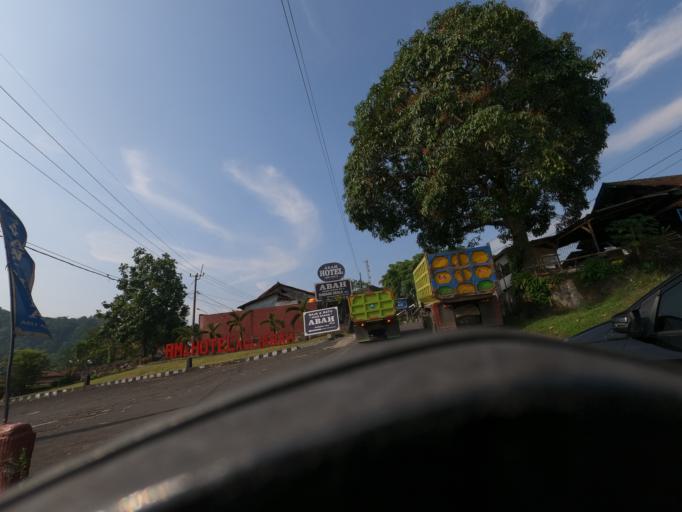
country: ID
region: West Java
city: Lembang
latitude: -6.6444
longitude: 107.7241
